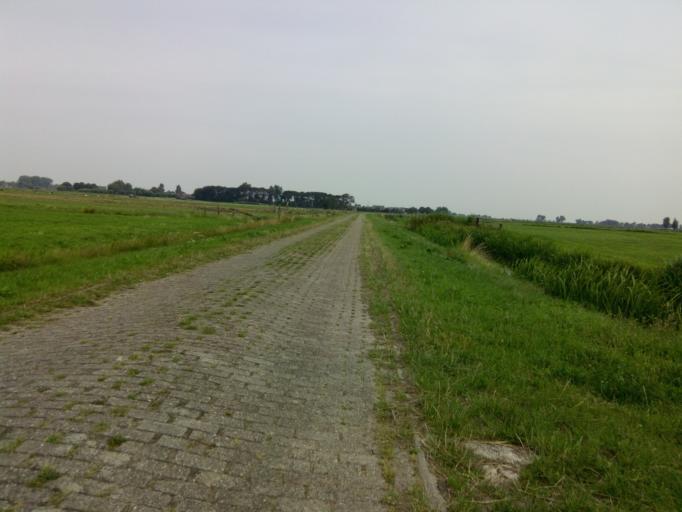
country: NL
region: Utrecht
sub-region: Gemeente Baarn
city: Baarn
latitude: 52.1965
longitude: 5.3223
